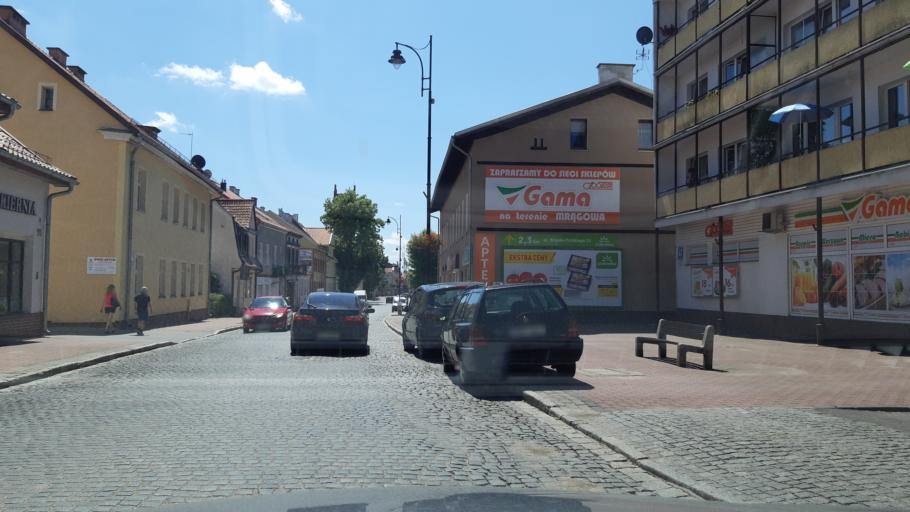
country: PL
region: Warmian-Masurian Voivodeship
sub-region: Powiat mragowski
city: Mragowo
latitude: 53.8754
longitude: 21.3041
